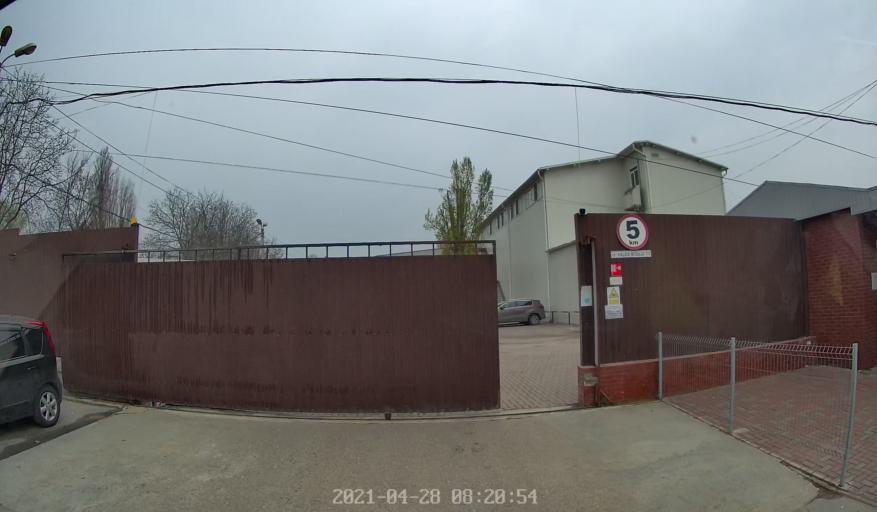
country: MD
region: Chisinau
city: Chisinau
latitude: 46.9890
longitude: 28.8924
